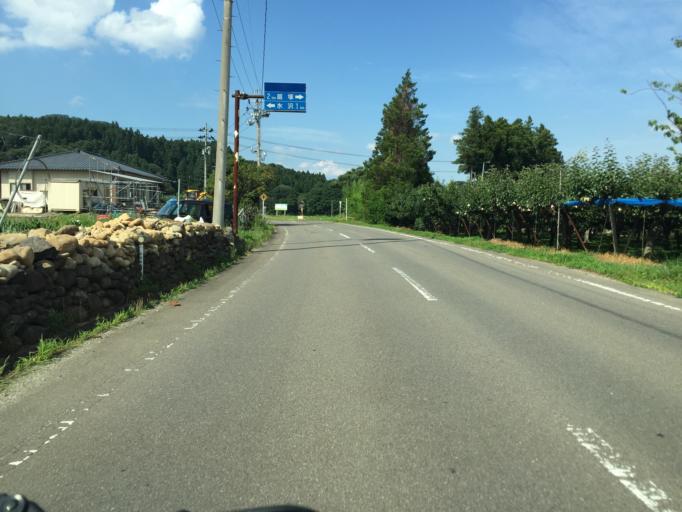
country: JP
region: Fukushima
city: Fukushima-shi
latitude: 37.7699
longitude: 140.3640
